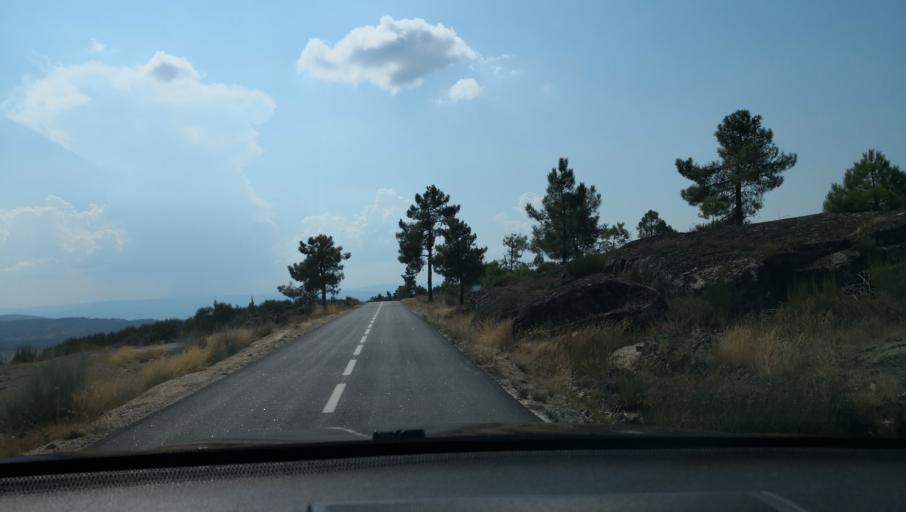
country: PT
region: Vila Real
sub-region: Sabrosa
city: Sabrosa
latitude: 41.2813
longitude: -7.6151
